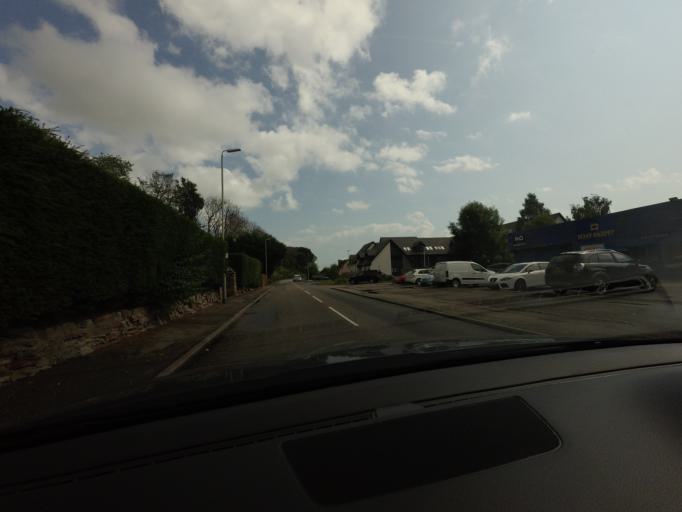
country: GB
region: Scotland
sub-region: Highland
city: Dingwall
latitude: 57.6026
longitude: -4.4244
